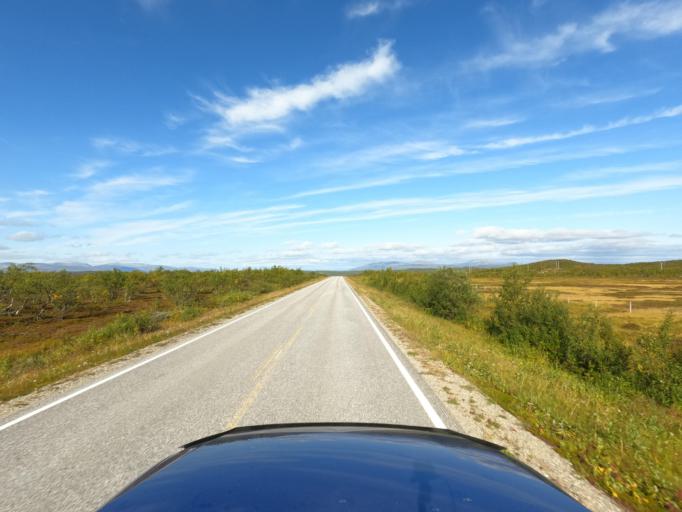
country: NO
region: Finnmark Fylke
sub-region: Karasjok
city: Karasjohka
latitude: 69.7206
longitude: 25.2376
